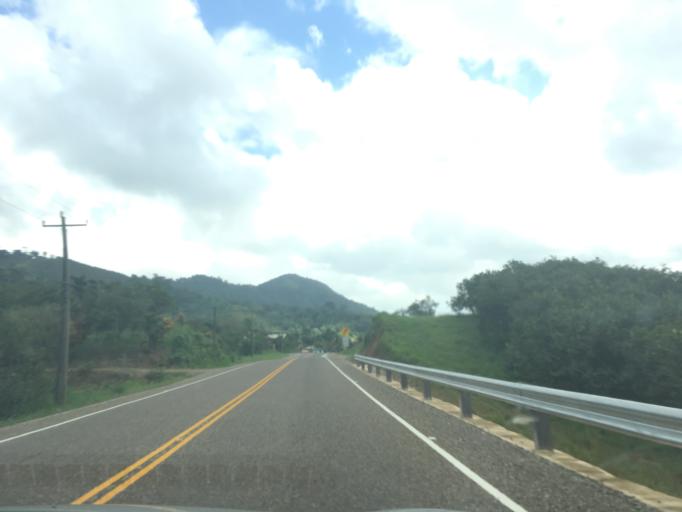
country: BZ
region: Stann Creek
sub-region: Dangriga
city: Dangriga
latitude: 16.9979
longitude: -88.4113
